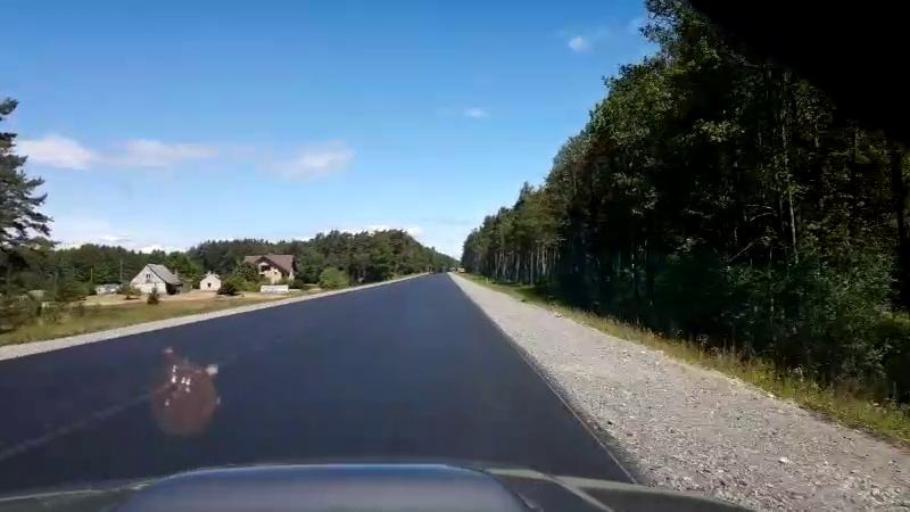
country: LV
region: Salacgrivas
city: Ainazi
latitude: 57.8361
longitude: 24.3461
